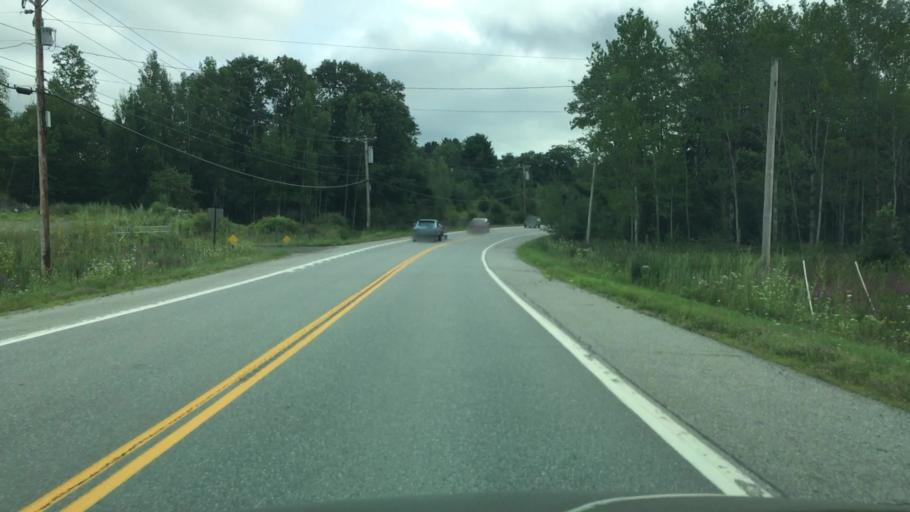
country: US
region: Maine
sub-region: Waldo County
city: Frankfort
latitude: 44.6253
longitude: -68.8690
